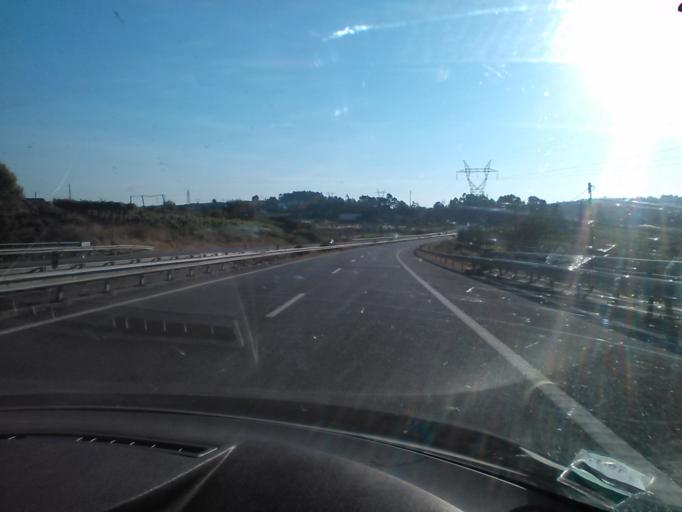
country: PT
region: Braga
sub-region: Vila Nova de Famalicao
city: Joane
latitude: 41.4062
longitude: -8.4336
